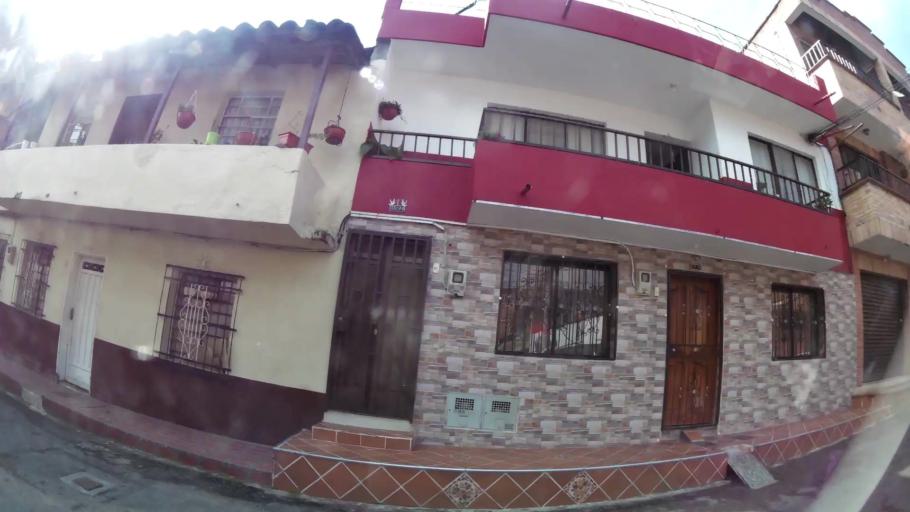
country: CO
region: Antioquia
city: La Estrella
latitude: 6.1907
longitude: -75.6422
